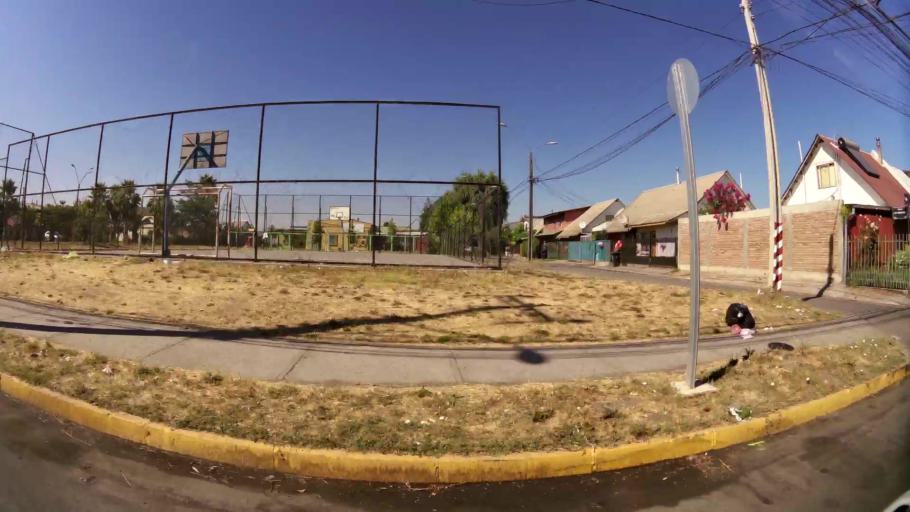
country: CL
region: Maule
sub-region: Provincia de Curico
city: Curico
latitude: -34.9800
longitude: -71.2579
